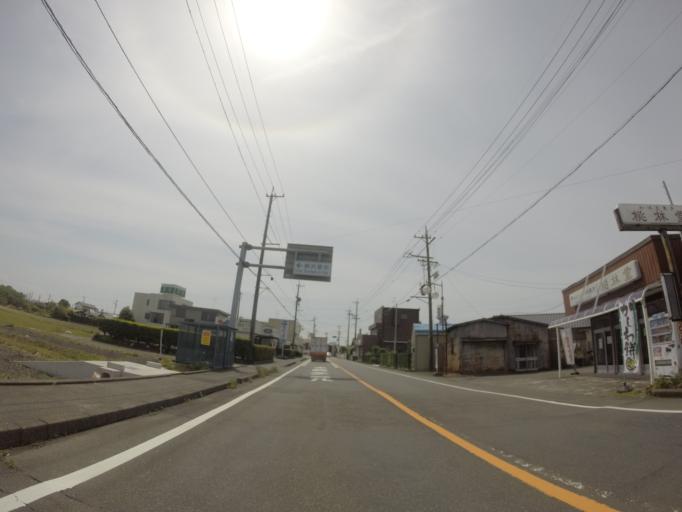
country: JP
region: Shizuoka
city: Fujieda
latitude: 34.8151
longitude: 138.2799
